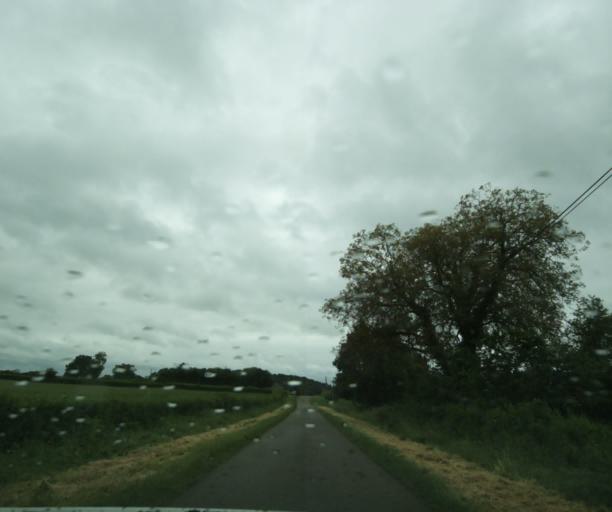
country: FR
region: Bourgogne
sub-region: Departement de Saone-et-Loire
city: Charolles
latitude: 46.4821
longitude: 4.2732
